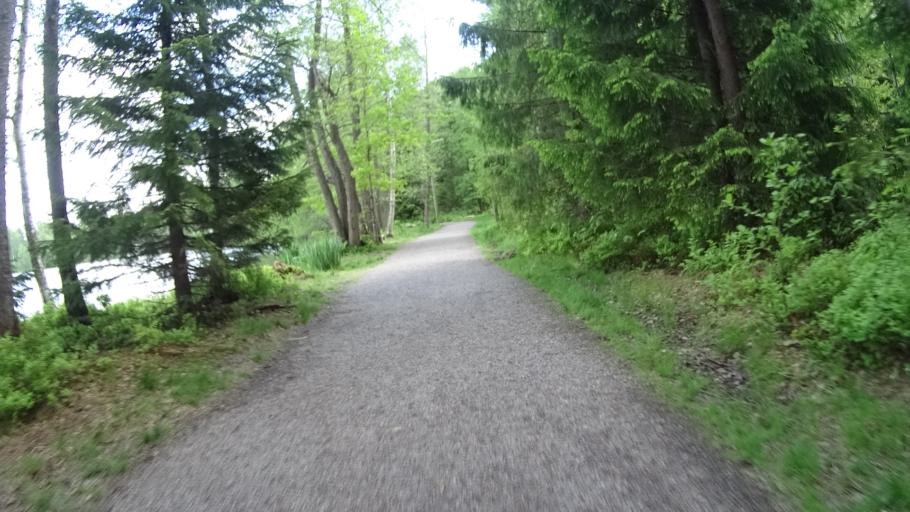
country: FI
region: Uusimaa
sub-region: Helsinki
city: Kauniainen
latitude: 60.2169
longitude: 24.7282
